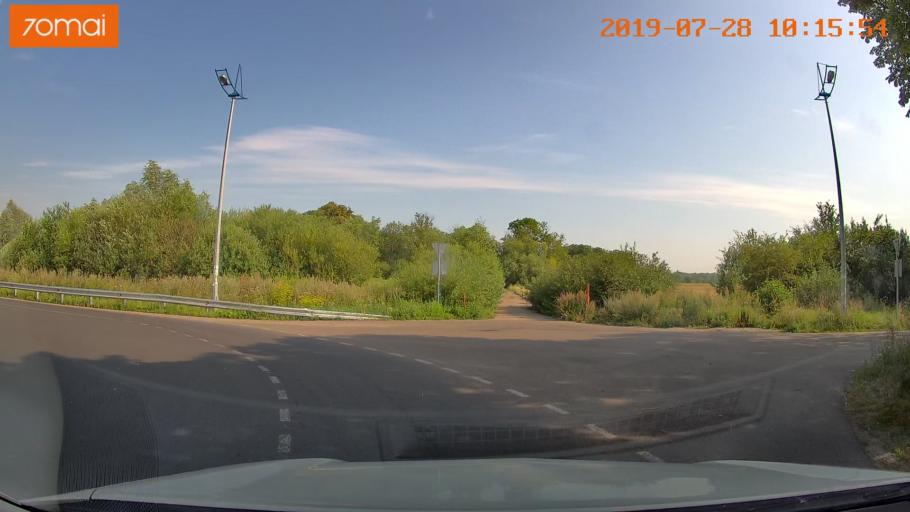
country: RU
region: Kaliningrad
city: Bol'shoe Isakovo
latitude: 54.7252
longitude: 20.6013
